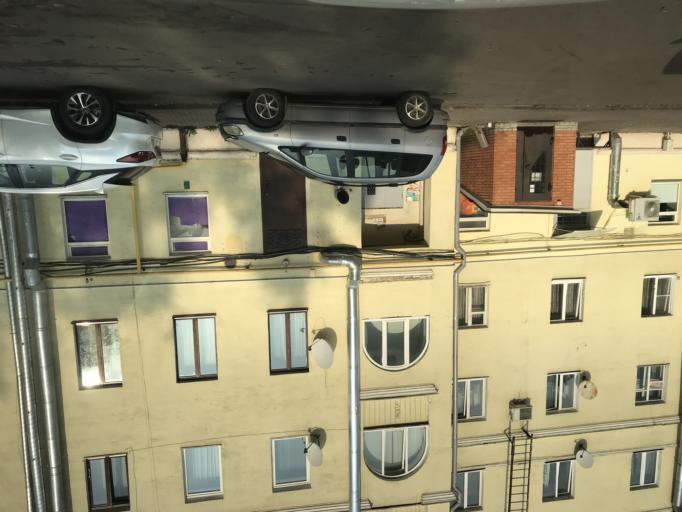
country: BY
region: Mogilev
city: Mahilyow
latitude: 53.9021
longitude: 30.3396
